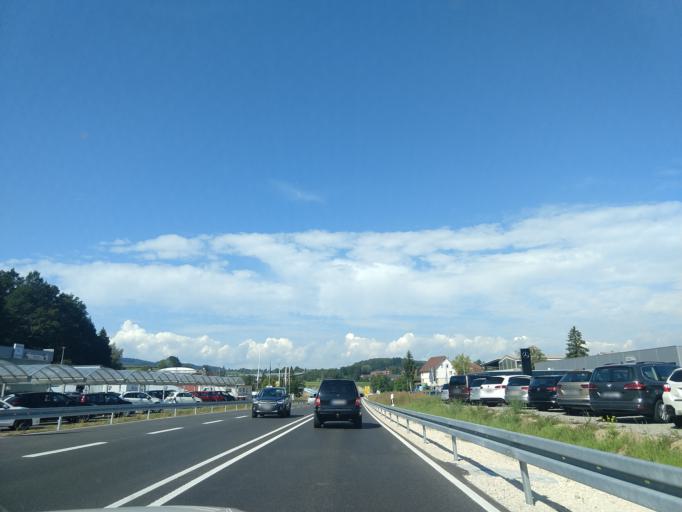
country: DE
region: Baden-Wuerttemberg
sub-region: Tuebingen Region
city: Uberlingen
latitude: 47.7720
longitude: 9.1864
